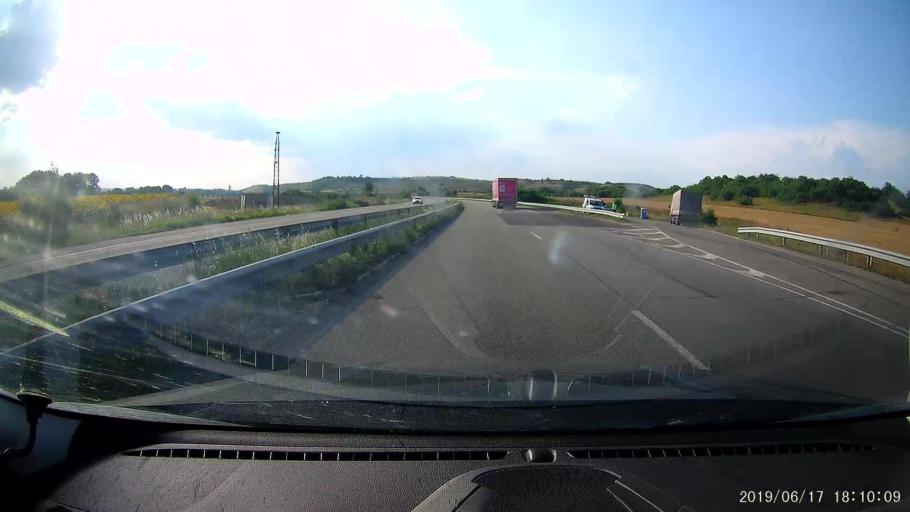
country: BG
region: Khaskovo
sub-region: Obshtina Lyubimets
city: Lyubimets
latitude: 41.8709
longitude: 26.0824
